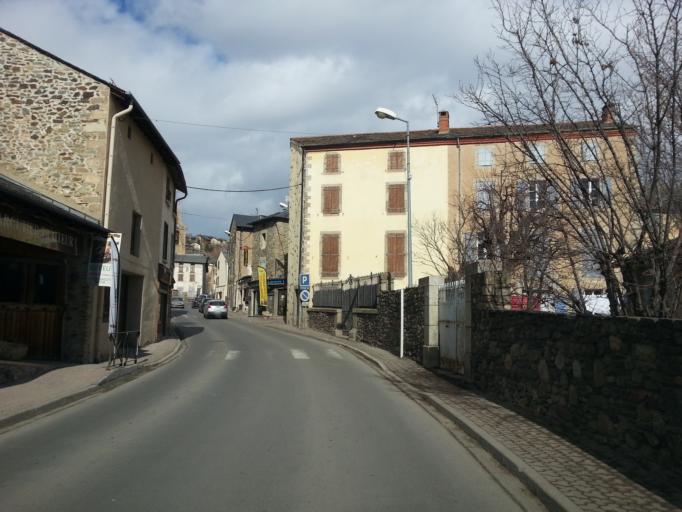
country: ES
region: Catalonia
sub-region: Provincia de Girona
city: Llivia
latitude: 42.4583
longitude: 2.0387
